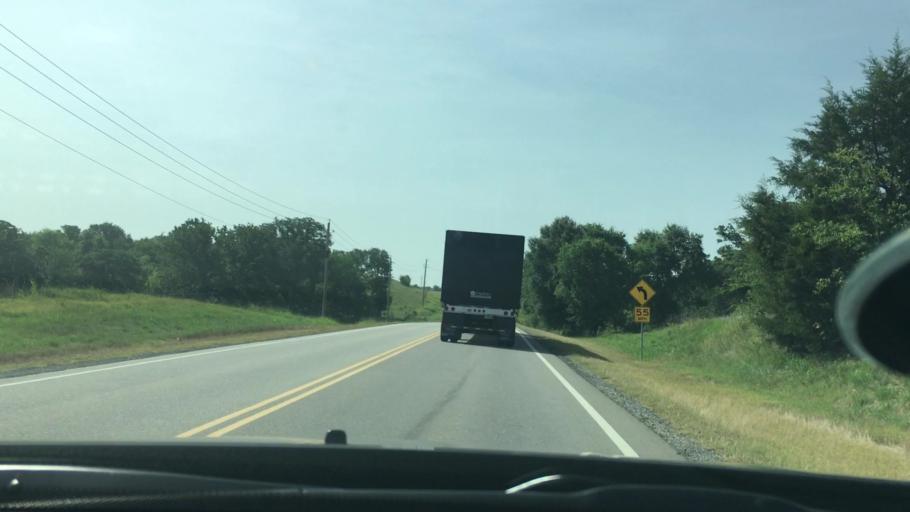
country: US
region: Oklahoma
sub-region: Atoka County
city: Atoka
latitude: 34.4068
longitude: -96.1803
